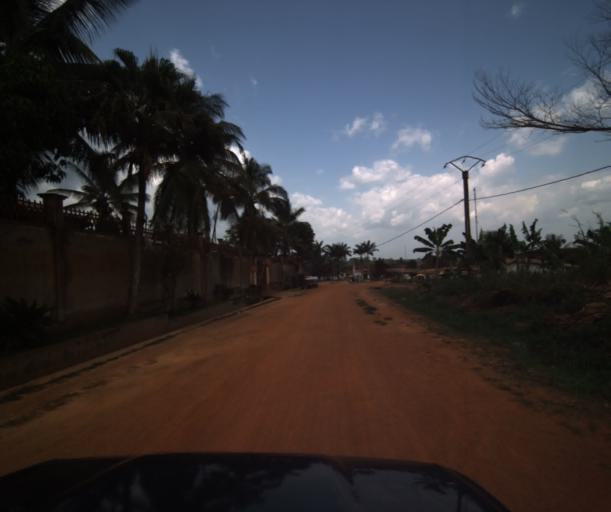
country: CM
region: Centre
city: Eseka
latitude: 3.5478
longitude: 11.0271
